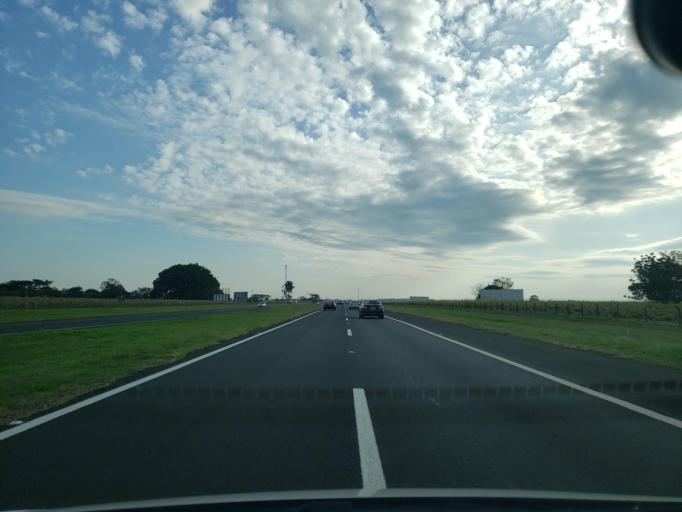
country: BR
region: Sao Paulo
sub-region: Guararapes
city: Guararapes
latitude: -21.2052
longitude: -50.6264
